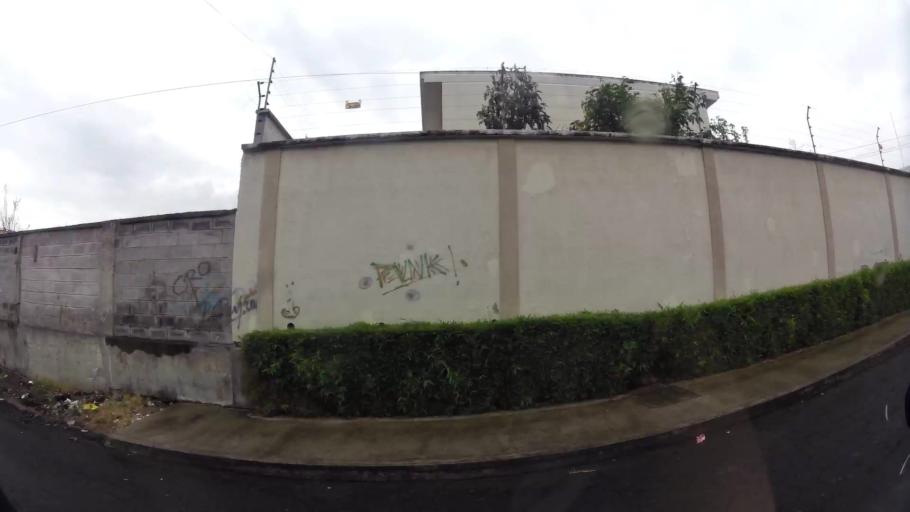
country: EC
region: Pichincha
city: Sangolqui
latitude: -0.2896
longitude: -78.4465
